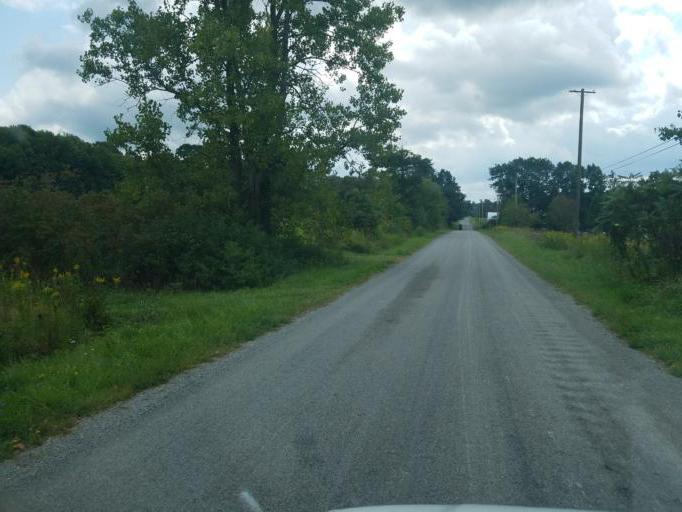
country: US
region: Ohio
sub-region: Geauga County
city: Middlefield
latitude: 41.5140
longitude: -81.0855
